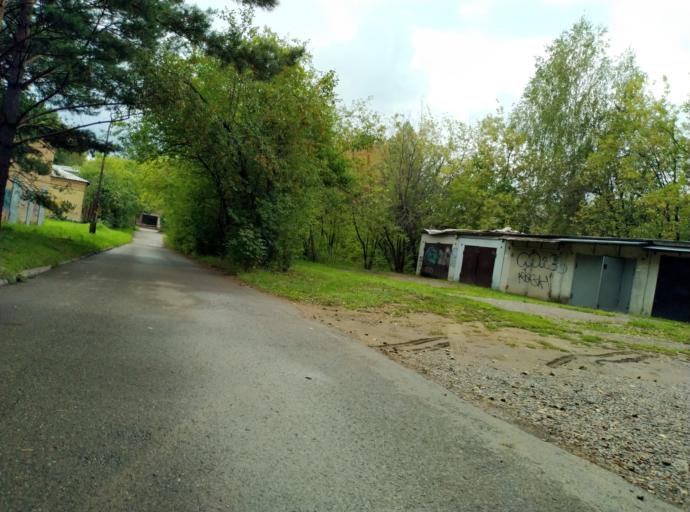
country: RU
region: Krasnoyarskiy
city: Krasnoyarsk
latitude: 55.9893
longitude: 92.7612
